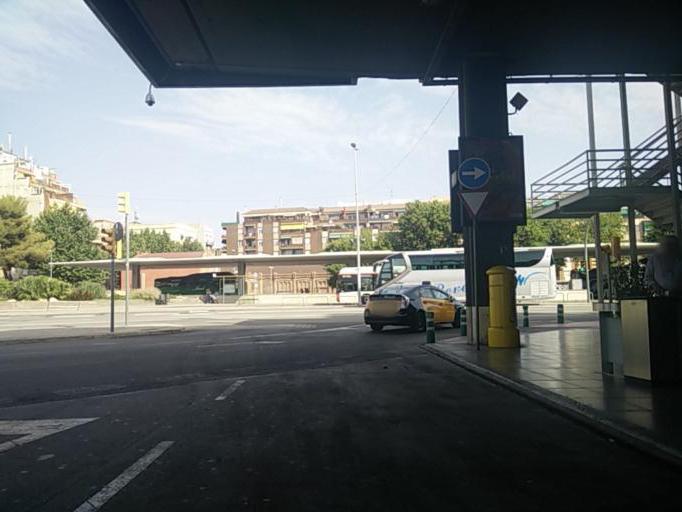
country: ES
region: Catalonia
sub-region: Provincia de Barcelona
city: les Corts
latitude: 41.3791
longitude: 2.1391
